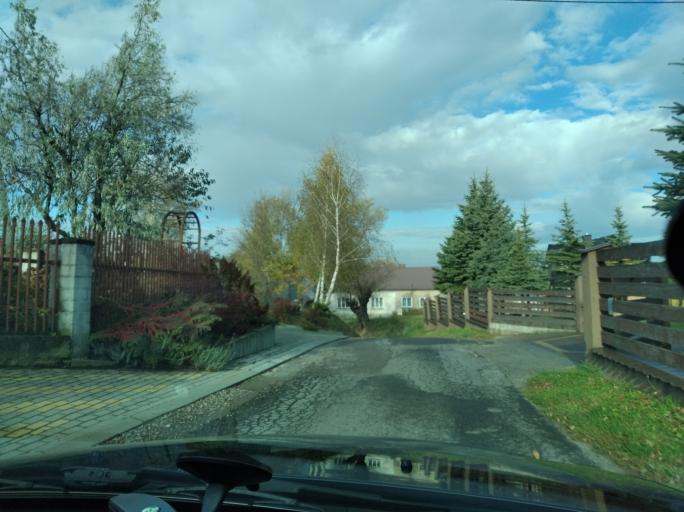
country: PL
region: Subcarpathian Voivodeship
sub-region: Powiat debicki
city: Debica
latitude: 50.0350
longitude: 21.4520
